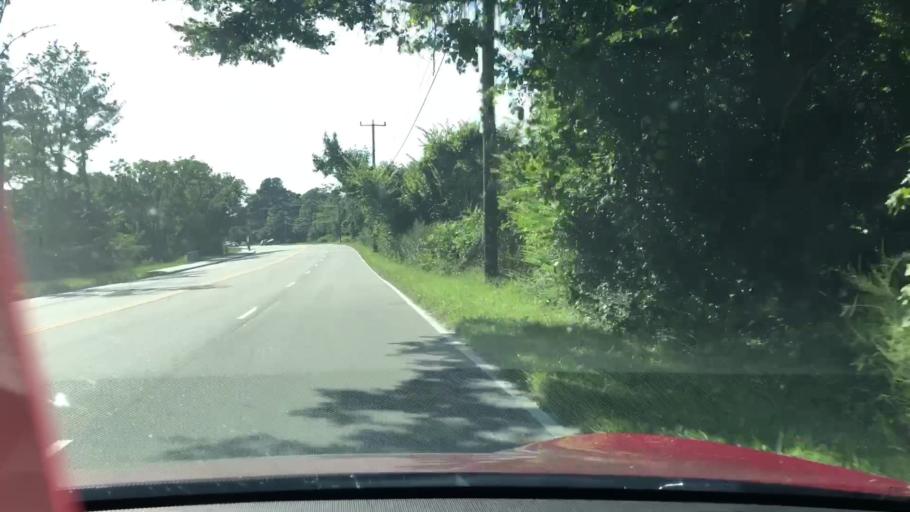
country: US
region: Virginia
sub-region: City of Virginia Beach
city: Virginia Beach
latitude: 36.8424
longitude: -76.0014
